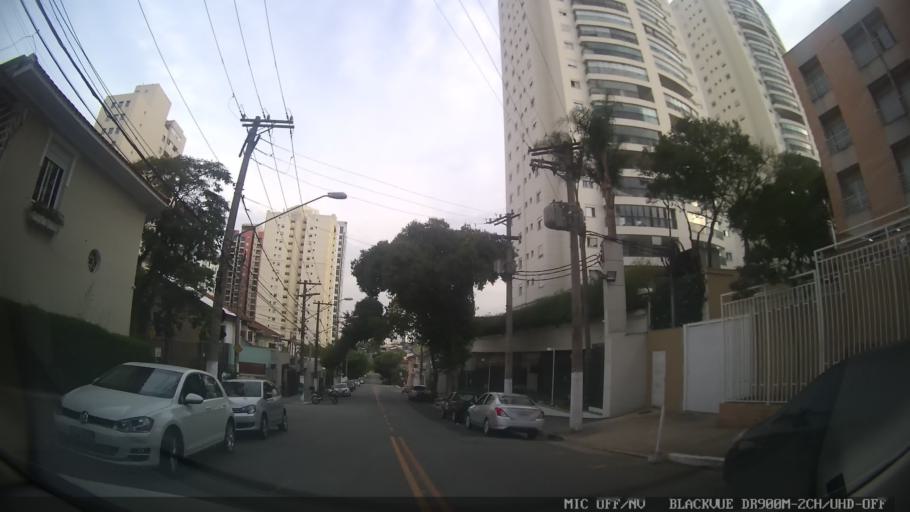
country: BR
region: Sao Paulo
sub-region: Sao Paulo
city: Sao Paulo
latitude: -23.5938
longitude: -46.6077
